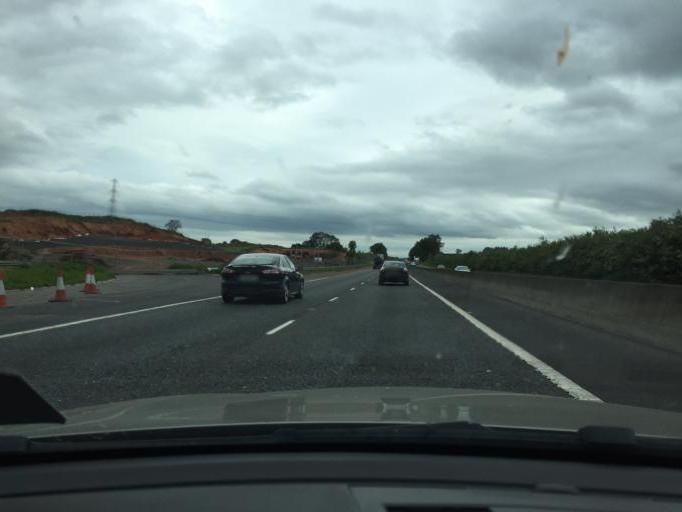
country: GB
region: Northern Ireland
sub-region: Lisburn District
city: Lisburn
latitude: 54.5275
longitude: -6.0022
